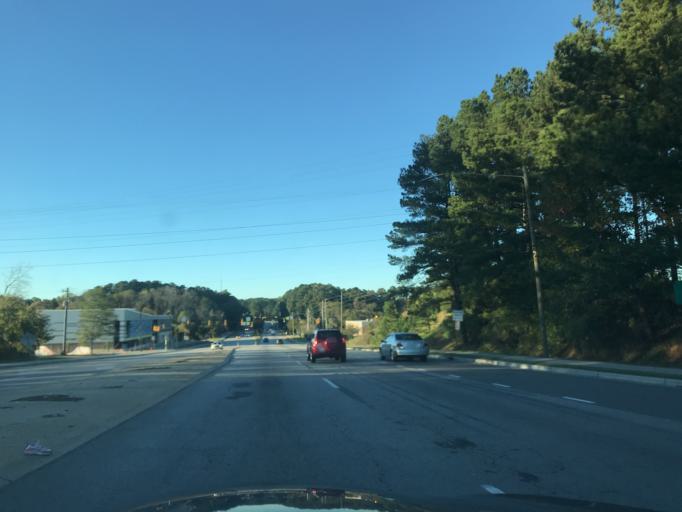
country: US
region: North Carolina
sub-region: Wake County
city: Raleigh
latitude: 35.7595
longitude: -78.6132
